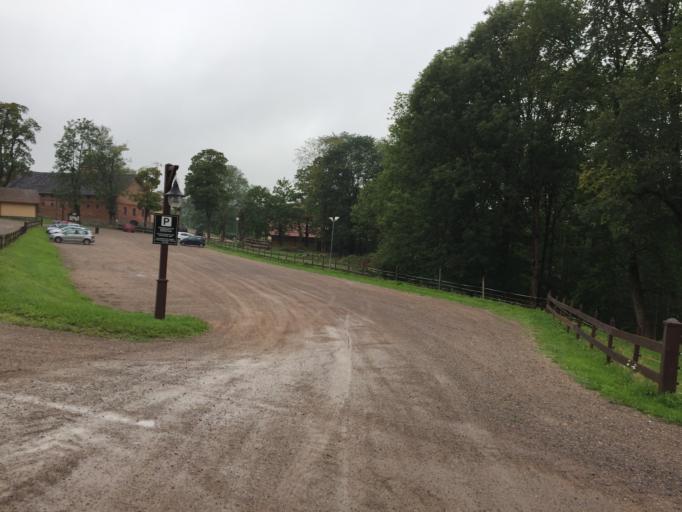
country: NO
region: Akershus
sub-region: Baerum
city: Lysaker
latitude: 59.9726
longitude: 10.6286
